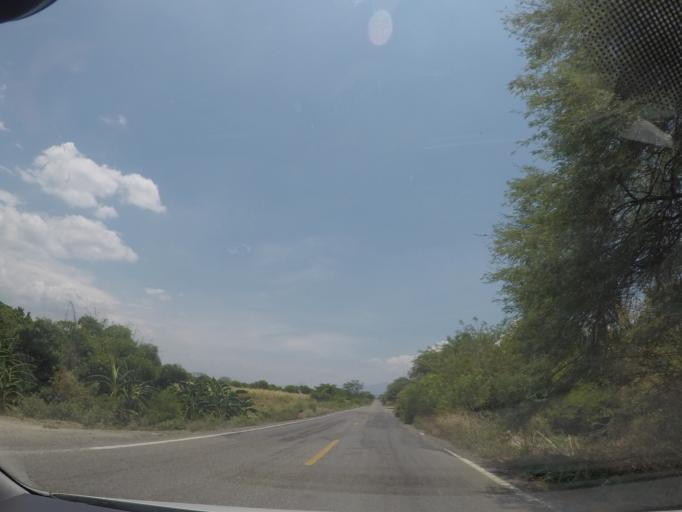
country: MX
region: Oaxaca
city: Santa Maria Jalapa del Marques
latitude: 16.4396
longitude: -95.4831
